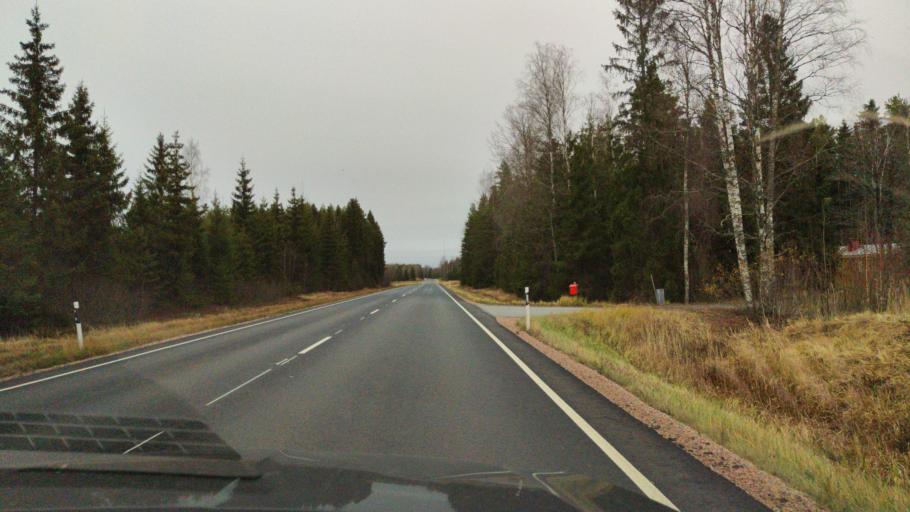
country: FI
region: Varsinais-Suomi
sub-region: Loimaa
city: Aura
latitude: 60.7081
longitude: 22.4427
